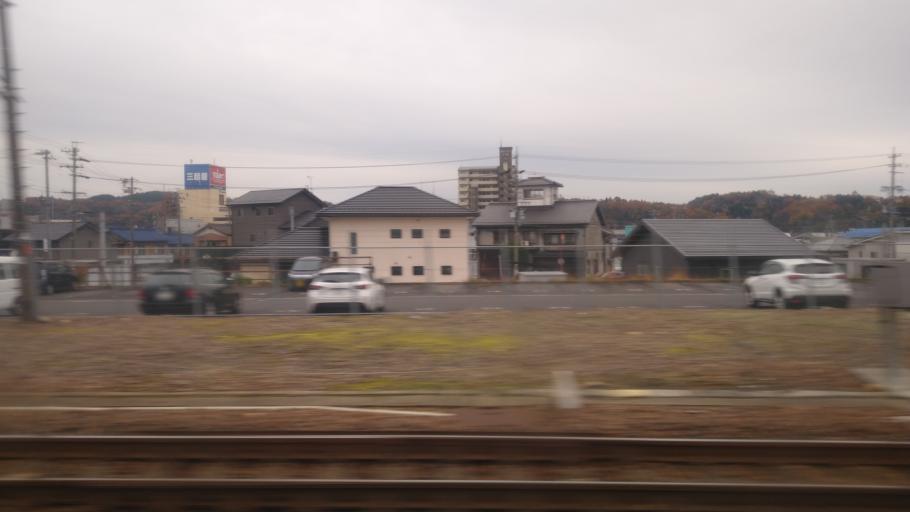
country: JP
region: Gifu
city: Toki
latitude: 35.3583
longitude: 137.1797
